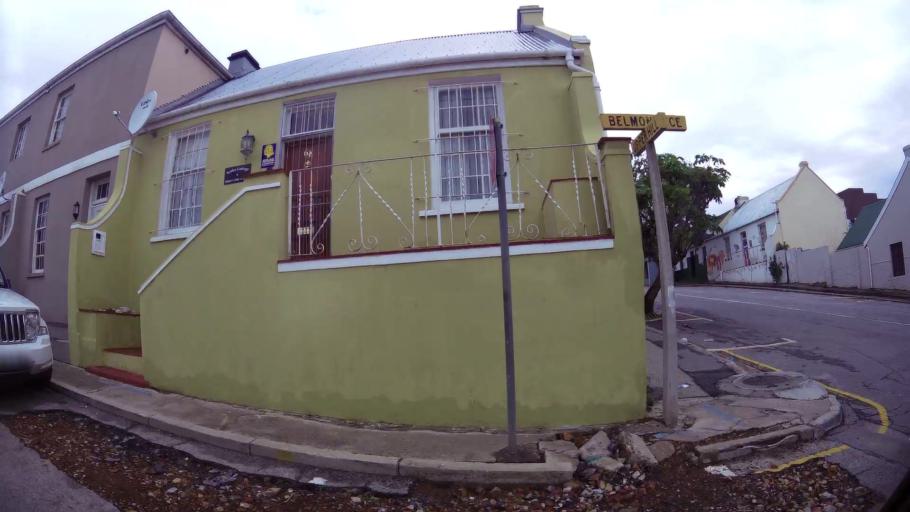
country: ZA
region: Eastern Cape
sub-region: Nelson Mandela Bay Metropolitan Municipality
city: Port Elizabeth
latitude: -33.9602
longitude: 25.6177
